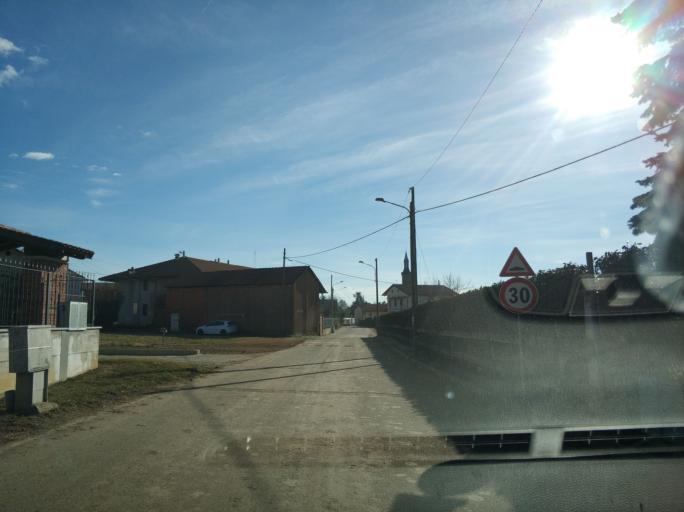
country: IT
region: Piedmont
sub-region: Provincia di Torino
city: San Carlo Canavese
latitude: 45.2514
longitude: 7.6077
